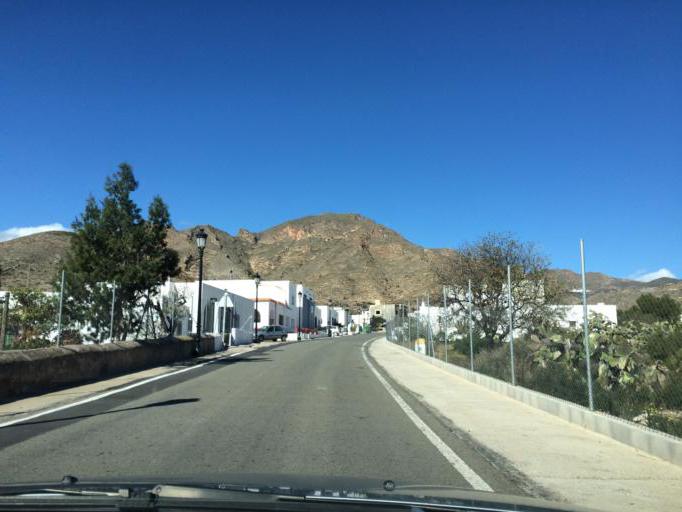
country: ES
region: Andalusia
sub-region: Provincia de Almeria
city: Nijar
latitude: 36.9591
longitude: -2.2066
